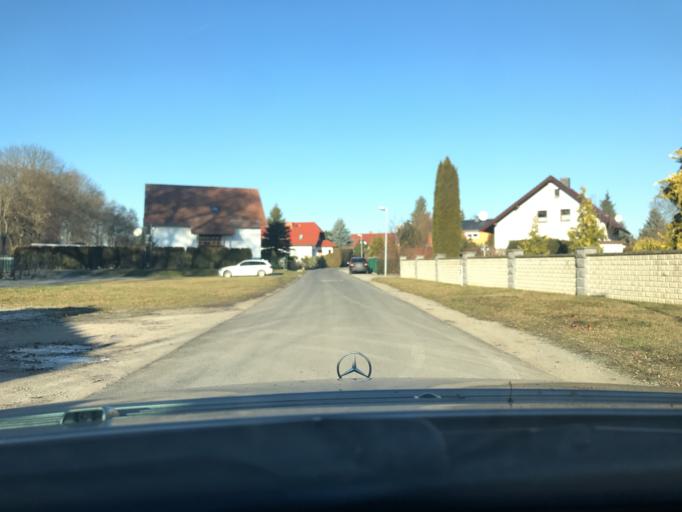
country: DE
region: Thuringia
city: Muehlhausen
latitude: 51.2263
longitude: 10.4492
